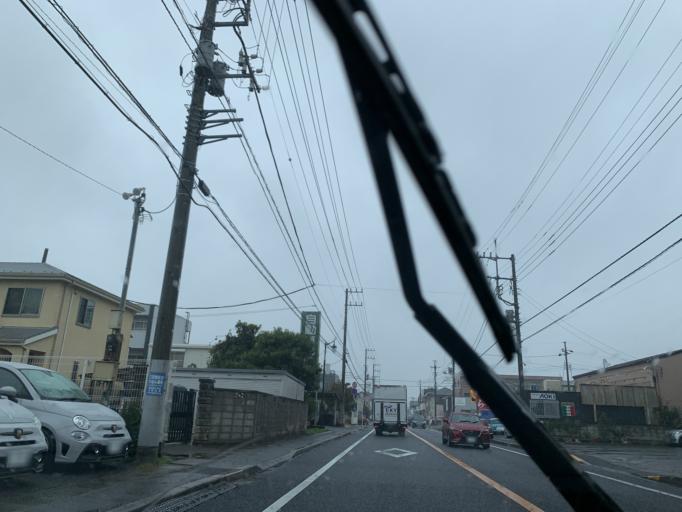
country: JP
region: Chiba
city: Nagareyama
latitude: 35.8621
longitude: 139.9027
